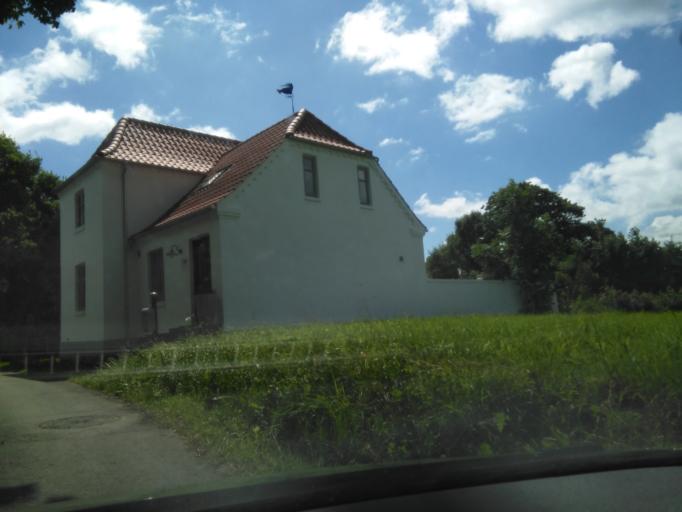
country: DK
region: Central Jutland
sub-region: Arhus Kommune
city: Logten
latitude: 56.1757
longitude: 10.3937
